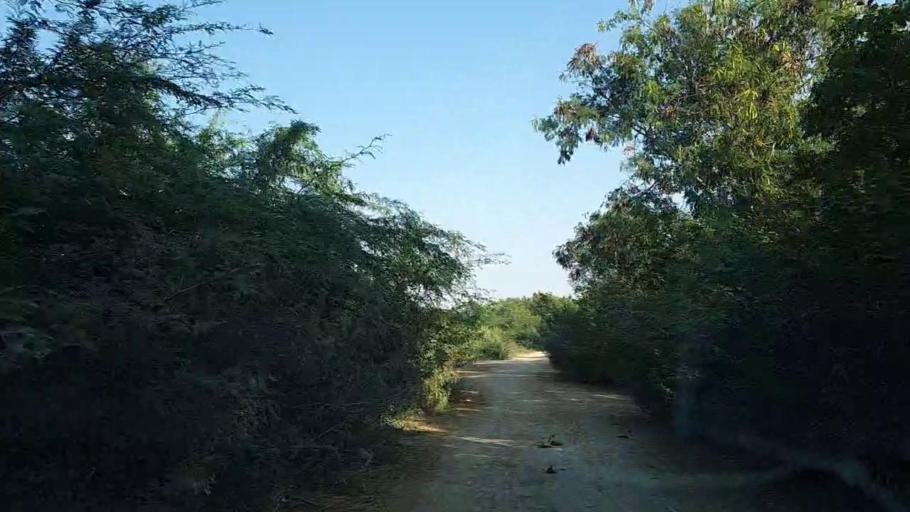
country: PK
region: Sindh
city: Chuhar Jamali
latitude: 24.5716
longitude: 68.0324
